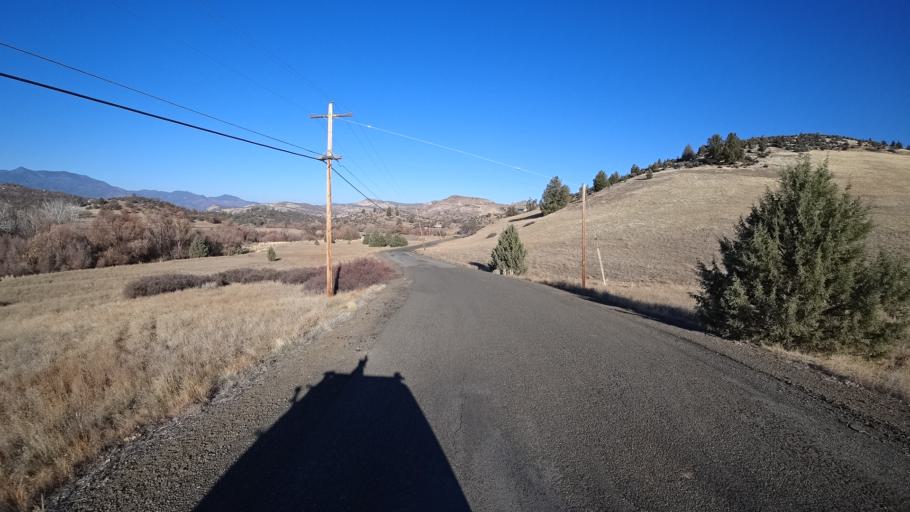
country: US
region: California
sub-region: Siskiyou County
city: Montague
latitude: 41.8885
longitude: -122.4794
